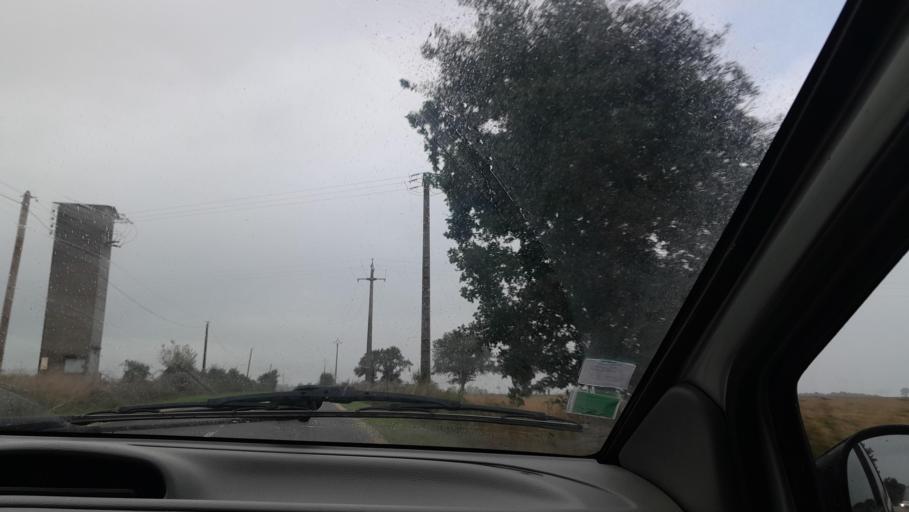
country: FR
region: Pays de la Loire
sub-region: Departement de la Mayenne
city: Congrier
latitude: 47.8145
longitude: -1.1473
